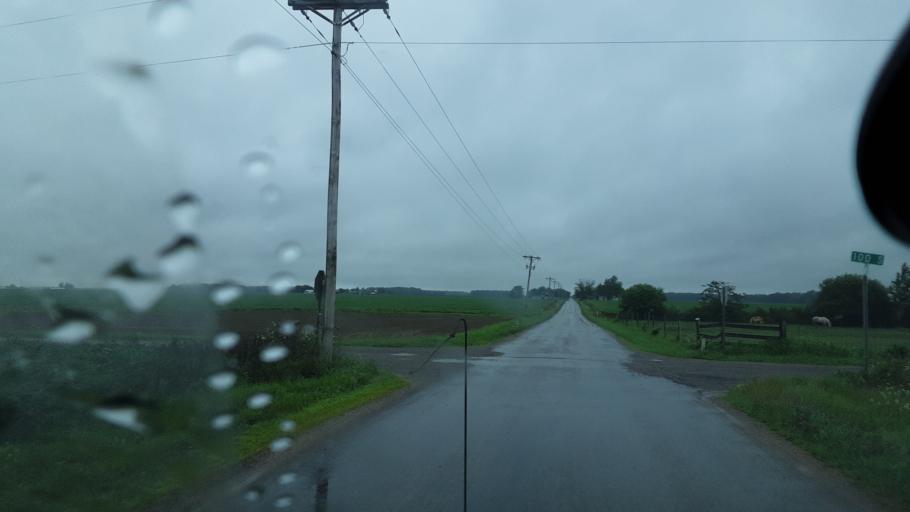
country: US
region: Indiana
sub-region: Adams County
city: Berne
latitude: 40.7318
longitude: -84.8544
